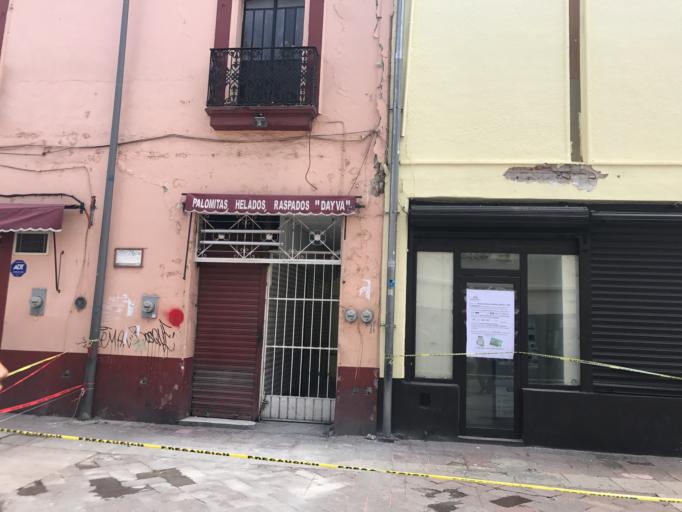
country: MX
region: Morelos
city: Cuautla Morelos
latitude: 18.8131
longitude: -98.9546
